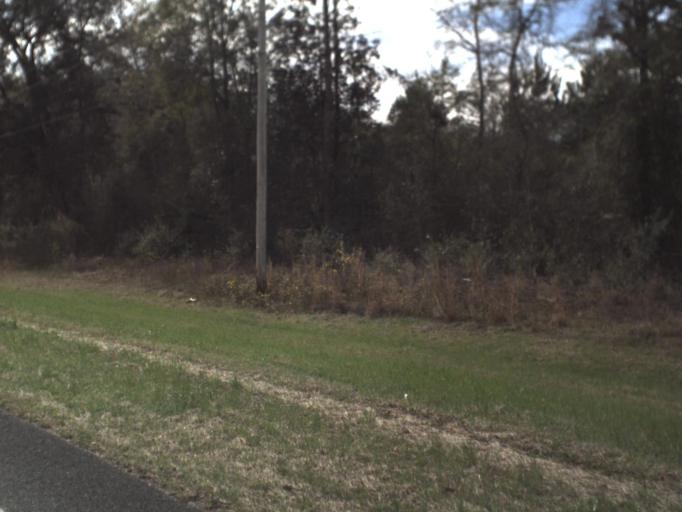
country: US
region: Florida
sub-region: Jackson County
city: Marianna
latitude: 30.7675
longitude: -85.3752
